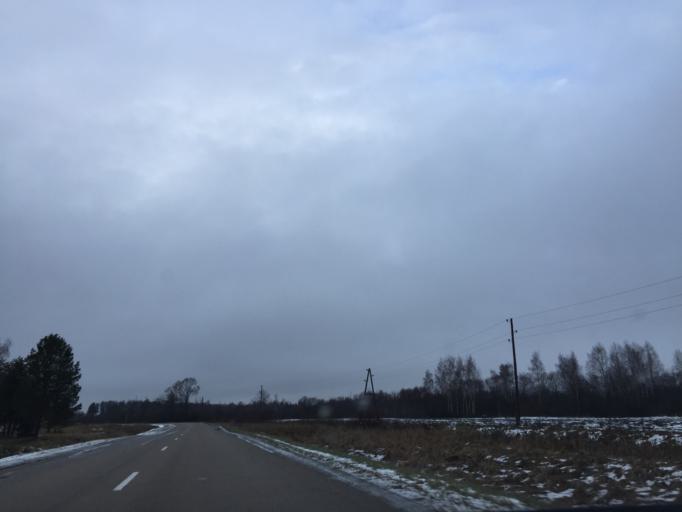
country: LV
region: Dagda
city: Dagda
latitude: 56.3067
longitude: 27.5135
